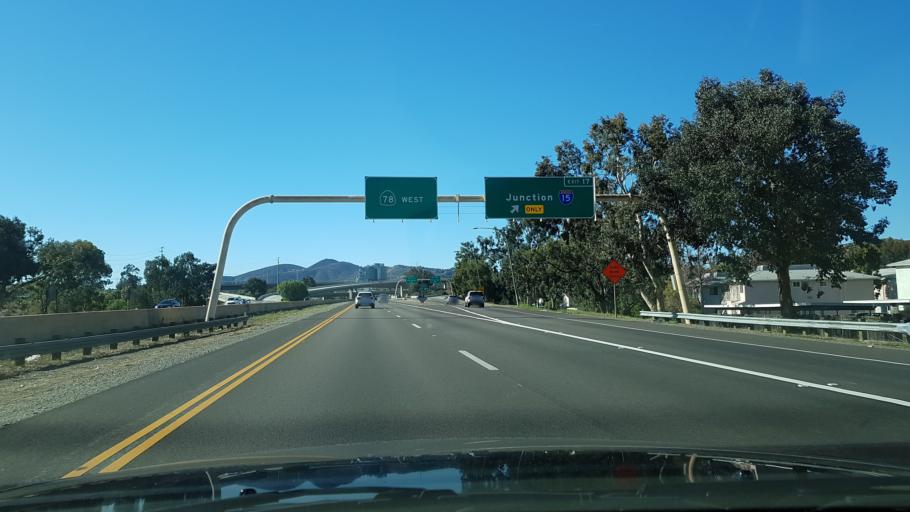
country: US
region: California
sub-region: San Diego County
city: Escondido
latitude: 33.1290
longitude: -117.0988
